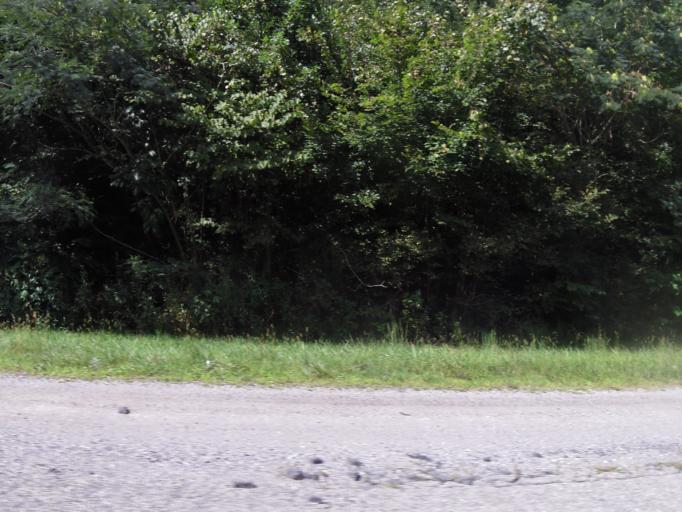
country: US
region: Kentucky
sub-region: Harlan County
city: Loyall
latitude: 36.8243
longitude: -83.4856
